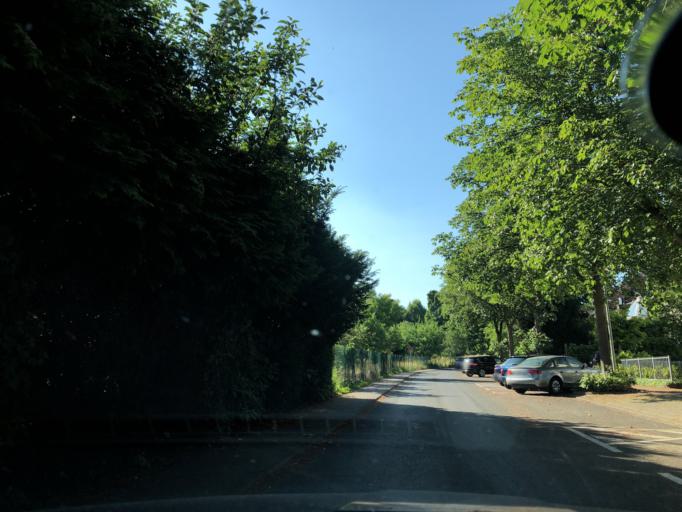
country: DE
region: Hesse
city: Sulzbach
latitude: 50.1290
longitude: 8.5233
